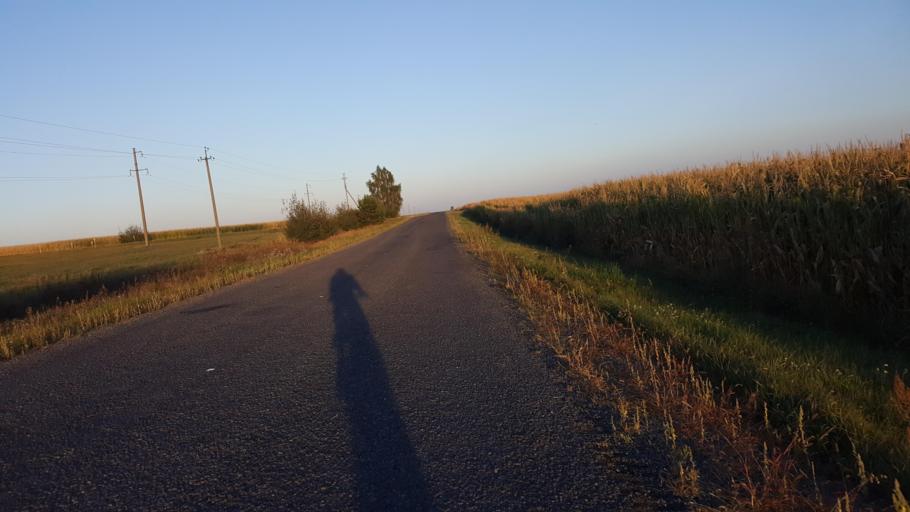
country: BY
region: Brest
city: Charnawchytsy
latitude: 52.2924
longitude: 23.5559
